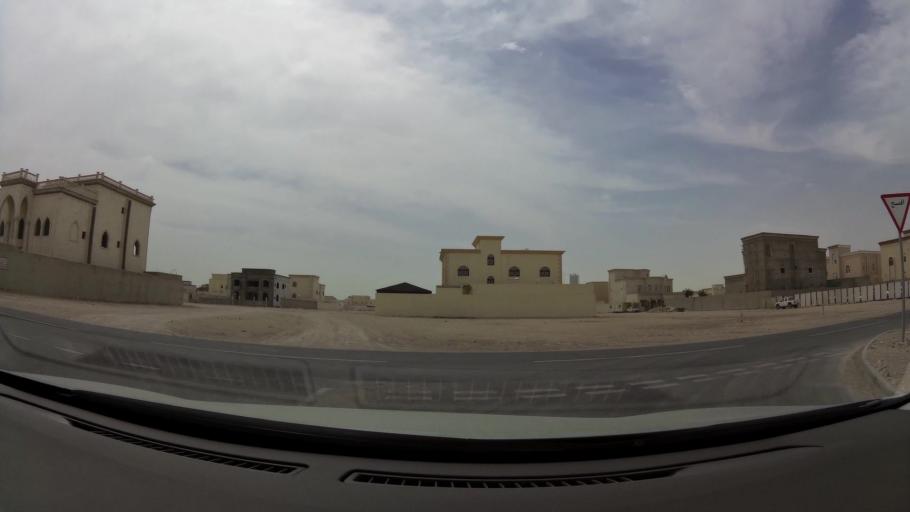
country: QA
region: Baladiyat ad Dawhah
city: Doha
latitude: 25.2116
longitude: 51.4668
